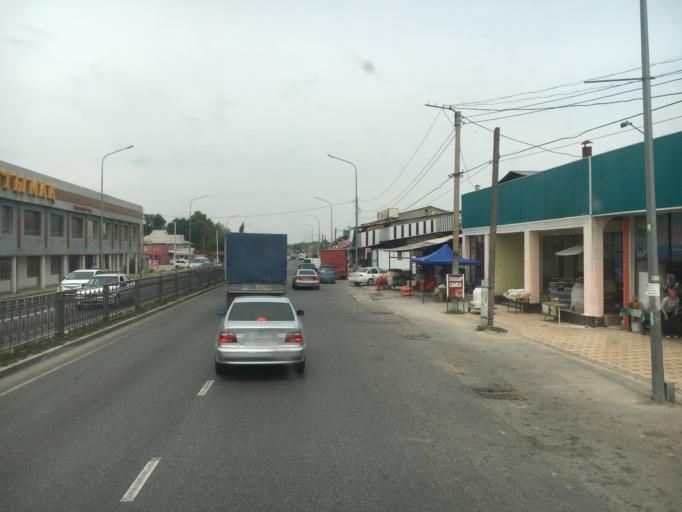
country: KZ
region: Ongtustik Qazaqstan
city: Shymkent
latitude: 42.3738
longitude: 69.5026
